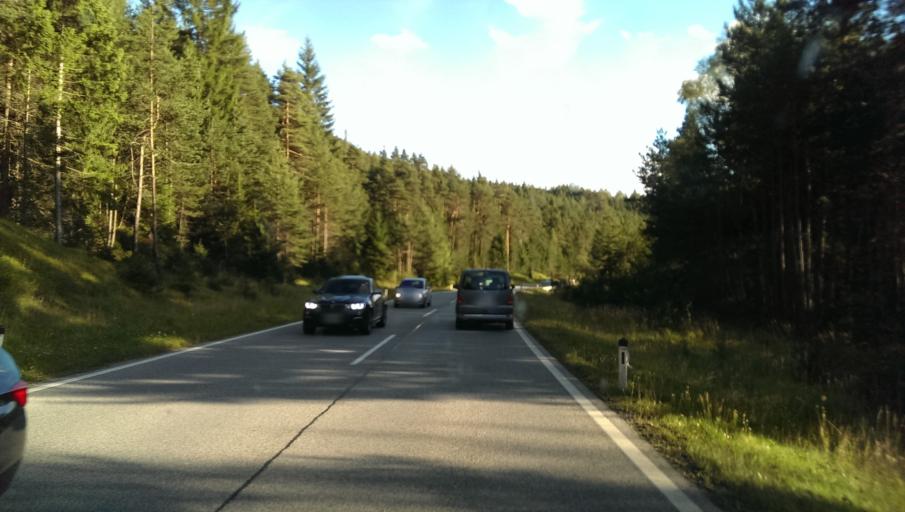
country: AT
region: Tyrol
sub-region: Politischer Bezirk Innsbruck Land
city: Reith bei Seefeld
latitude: 47.3103
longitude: 11.2020
